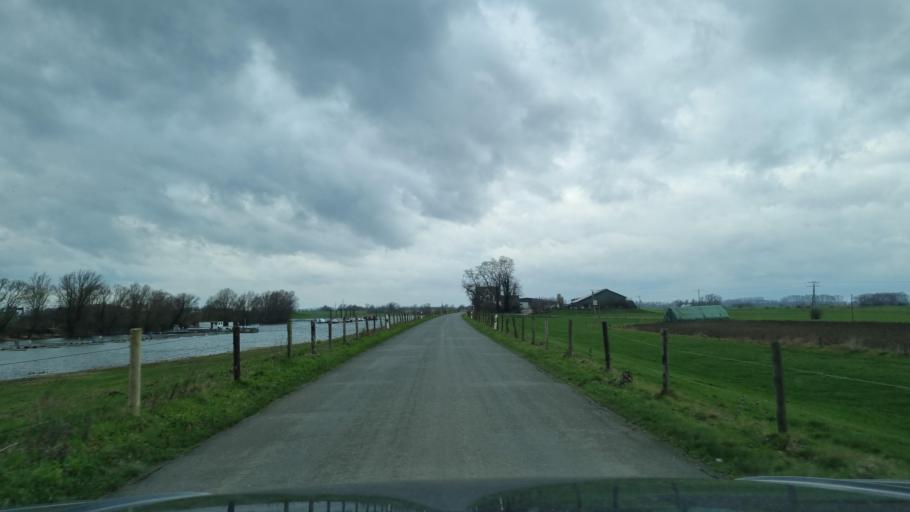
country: DE
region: North Rhine-Westphalia
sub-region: Regierungsbezirk Dusseldorf
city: Kleve
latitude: 51.8300
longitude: 6.1471
